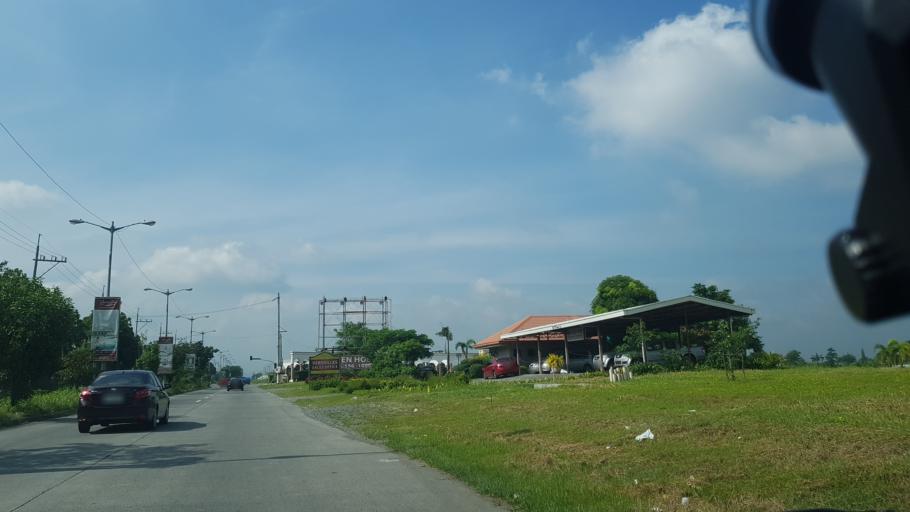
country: PH
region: Calabarzon
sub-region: Province of Laguna
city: San Pedro
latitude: 14.3984
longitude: 121.0117
